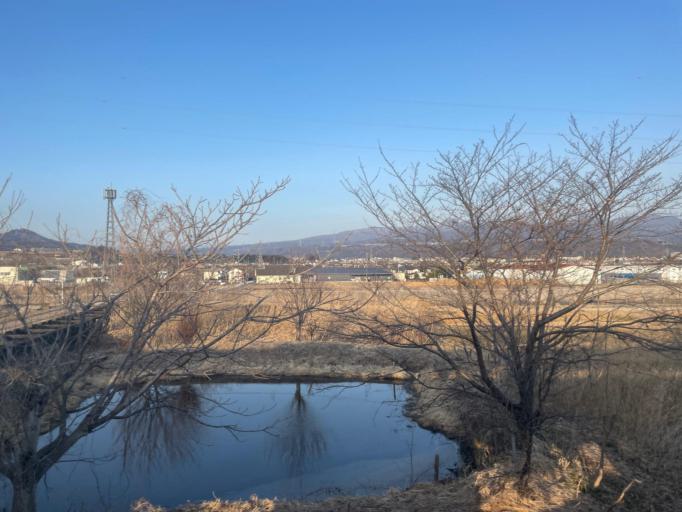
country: JP
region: Gunma
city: Shibukawa
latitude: 36.5170
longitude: 138.9940
